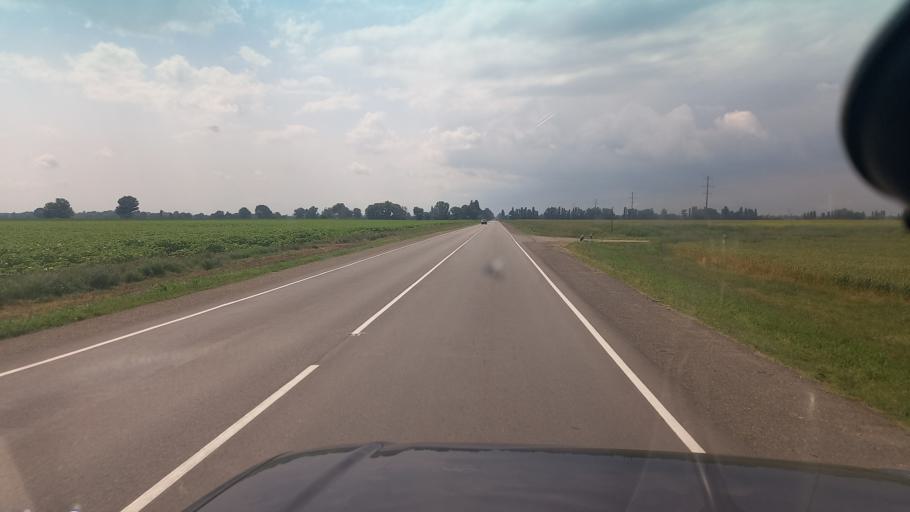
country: RU
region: Adygeya
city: Koshekhabl'
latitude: 44.9078
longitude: 40.4584
